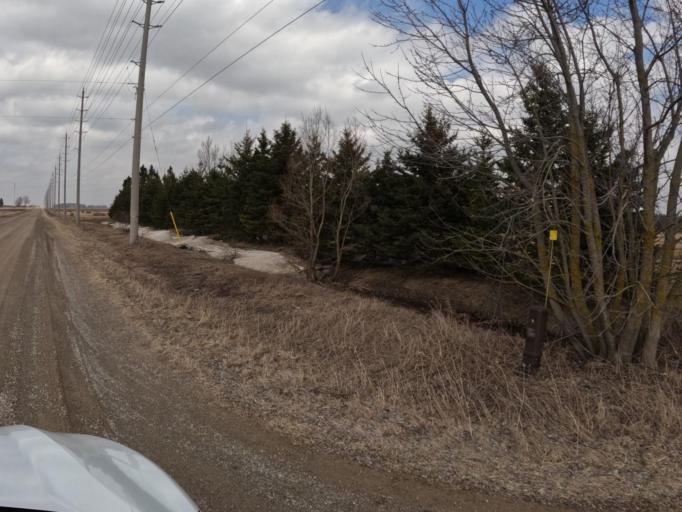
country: CA
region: Ontario
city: Shelburne
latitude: 44.0360
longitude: -80.3165
